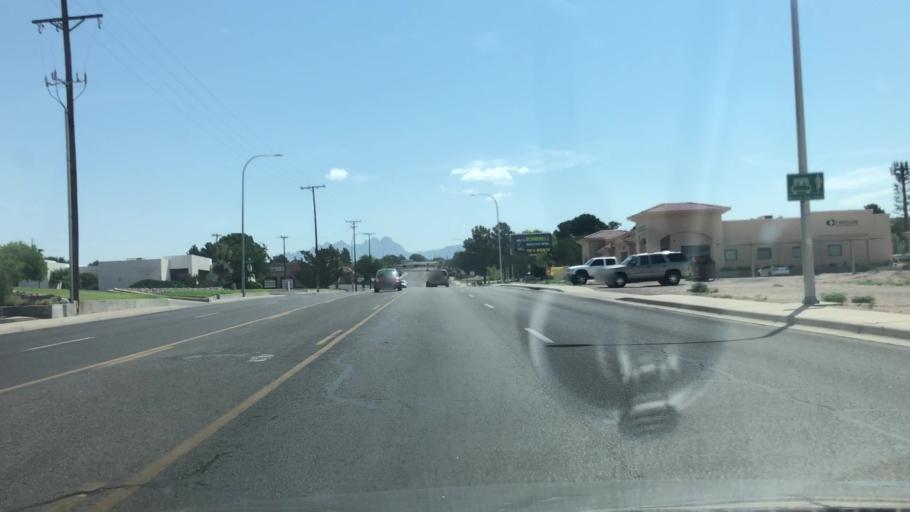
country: US
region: New Mexico
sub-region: Dona Ana County
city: University Park
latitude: 32.2992
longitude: -106.7400
